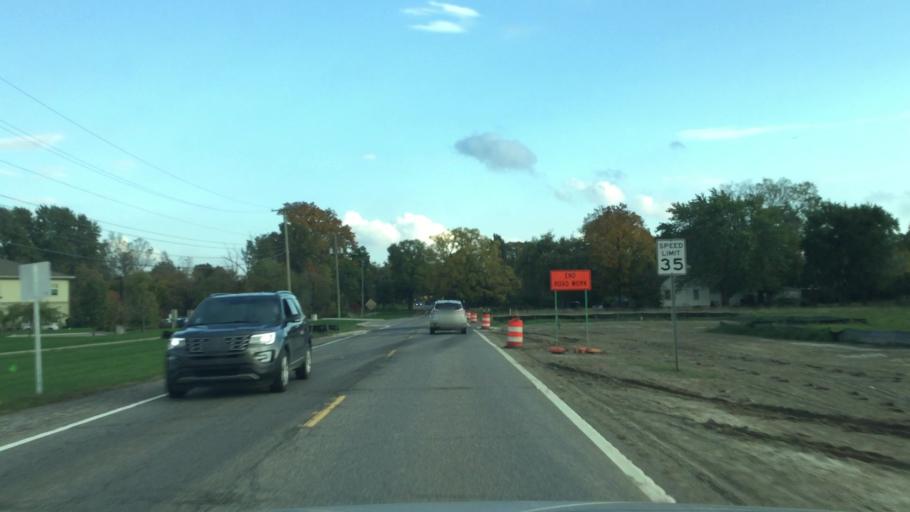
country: US
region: Michigan
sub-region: Oakland County
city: Wolverine Lake
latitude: 42.6449
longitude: -83.5002
